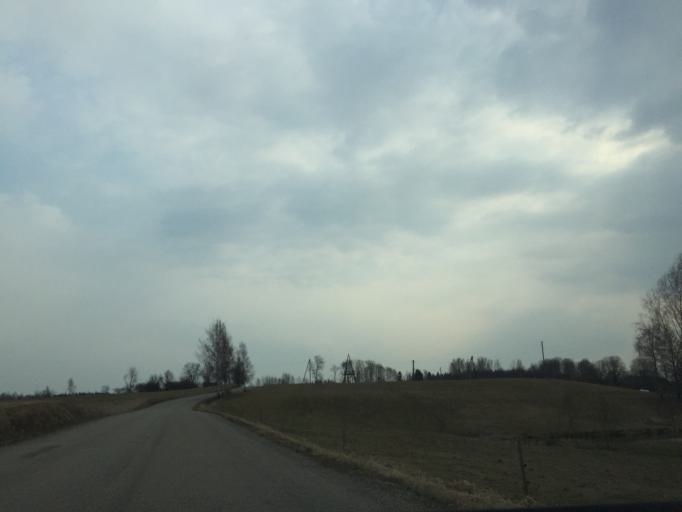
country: LV
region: Priekuli
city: Priekuli
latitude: 57.2366
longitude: 25.3785
